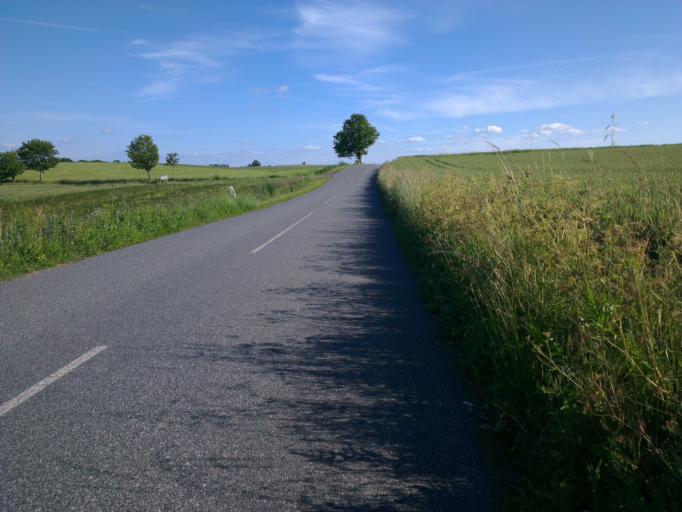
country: DK
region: Capital Region
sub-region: Frederikssund Kommune
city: Skibby
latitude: 55.7626
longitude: 11.9824
